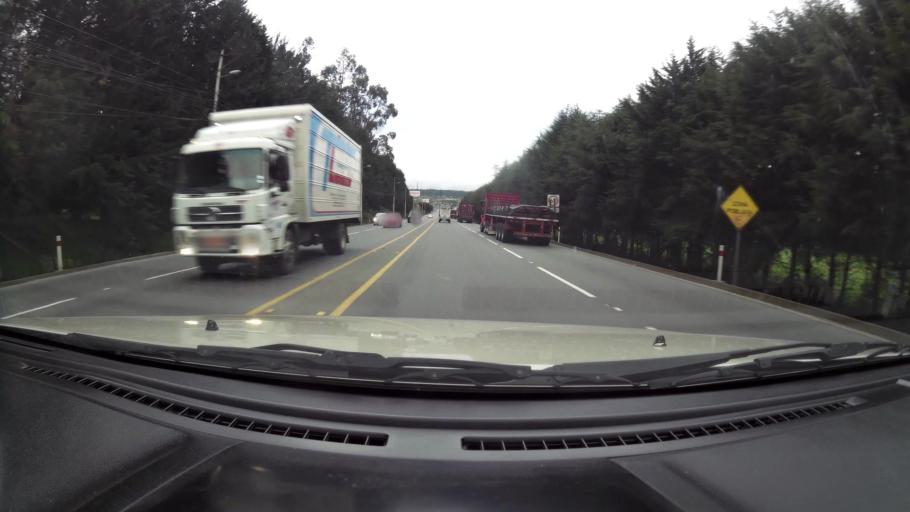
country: EC
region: Pichincha
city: Machachi
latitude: -0.4505
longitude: -78.5949
